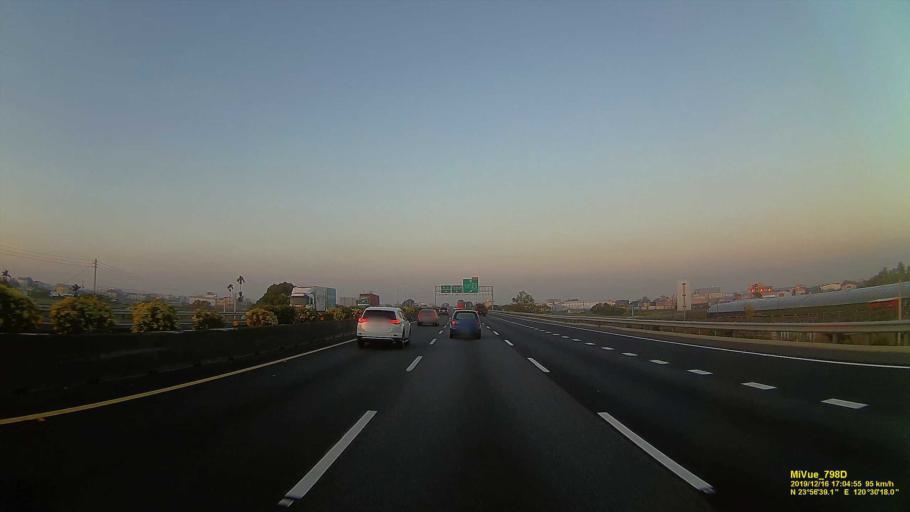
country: TW
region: Taiwan
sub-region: Changhua
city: Chang-hua
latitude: 23.9446
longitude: 120.5052
